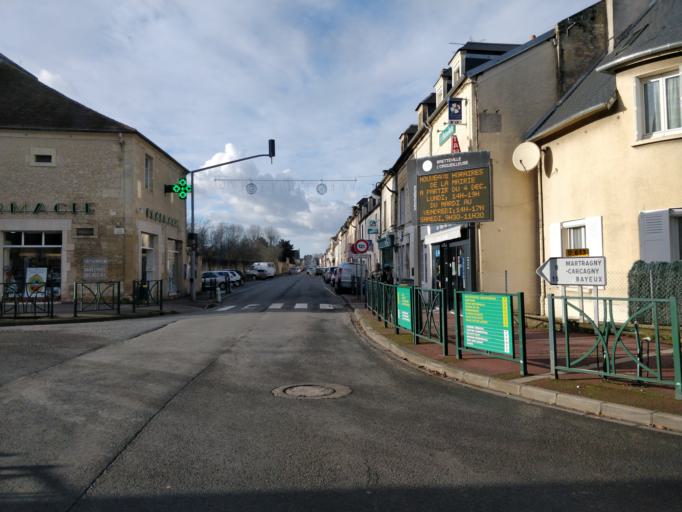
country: FR
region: Lower Normandy
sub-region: Departement du Calvados
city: Saint-Manvieu-Norrey
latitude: 49.2099
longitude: -0.5107
